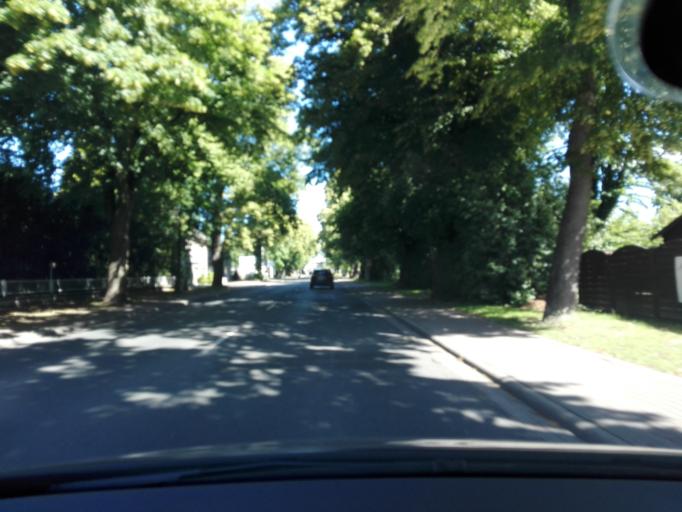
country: DE
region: North Rhine-Westphalia
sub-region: Regierungsbezirk Arnsberg
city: Unna
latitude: 51.5601
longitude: 7.6813
